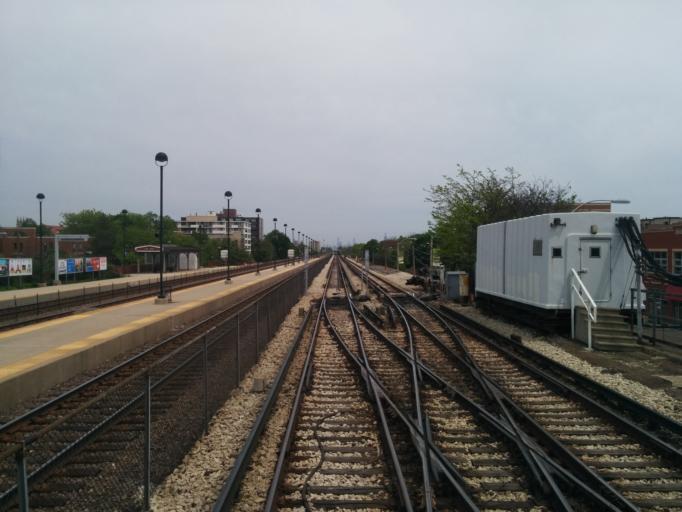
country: US
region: Illinois
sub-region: Cook County
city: Forest Park
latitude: 41.8870
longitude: -87.8021
